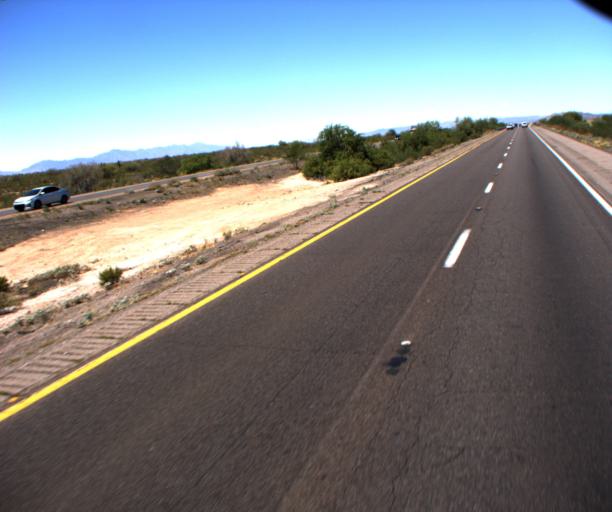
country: US
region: Arizona
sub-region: Pinal County
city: Sacaton
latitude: 33.0624
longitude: -111.7991
